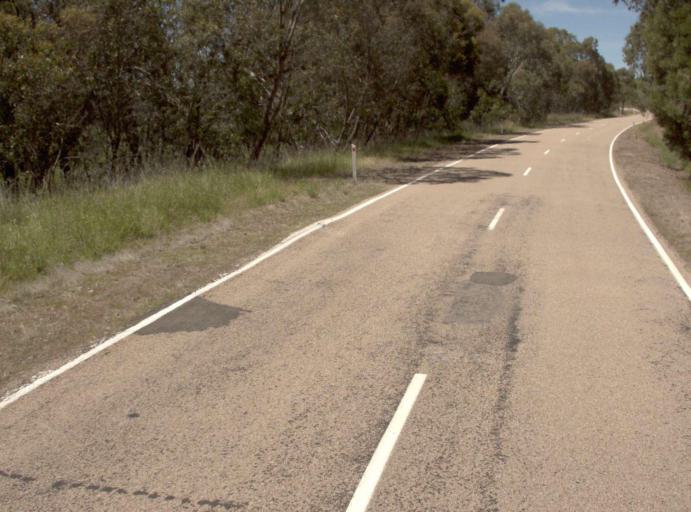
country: AU
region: Victoria
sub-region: East Gippsland
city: Lakes Entrance
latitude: -37.2030
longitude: 148.2695
